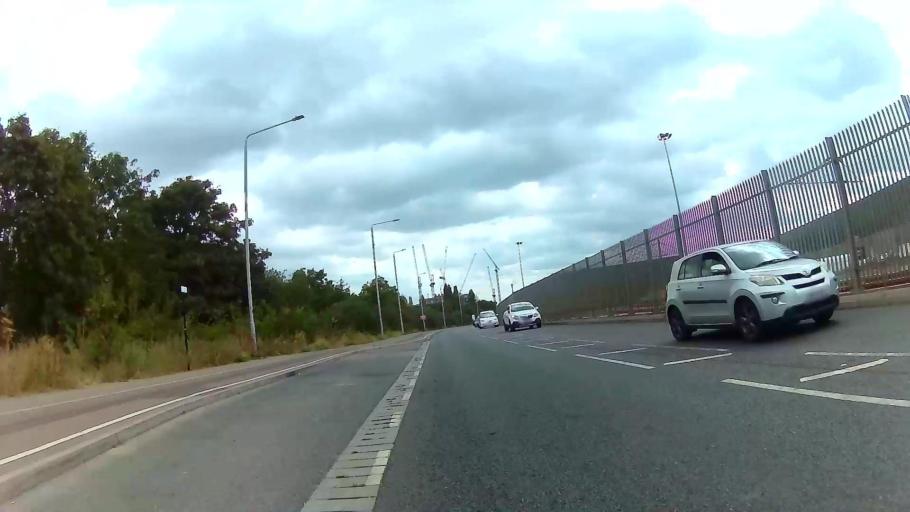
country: GB
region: England
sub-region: Greater London
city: Hackney
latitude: 51.5617
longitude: -0.0240
